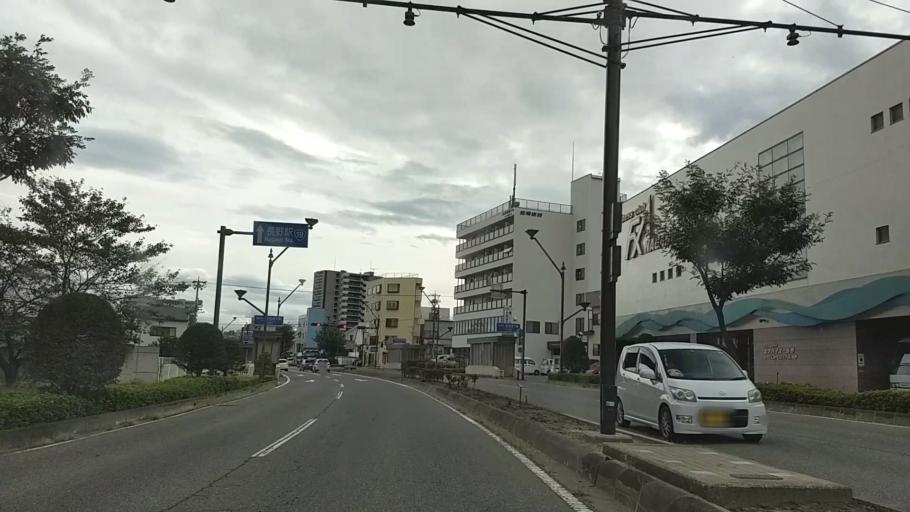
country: JP
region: Nagano
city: Nagano-shi
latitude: 36.6597
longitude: 138.1941
